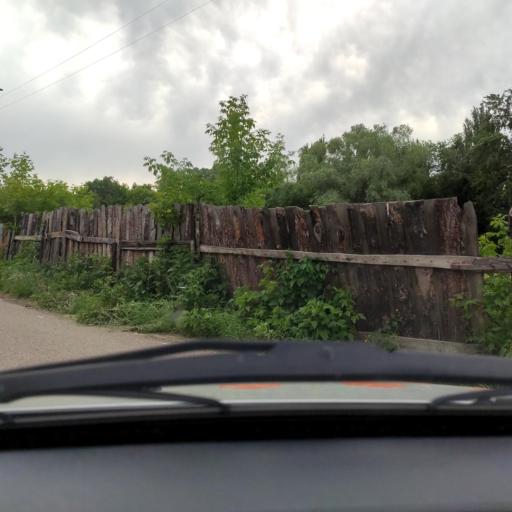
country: RU
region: Bashkortostan
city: Sterlitamak
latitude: 53.6249
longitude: 55.9566
